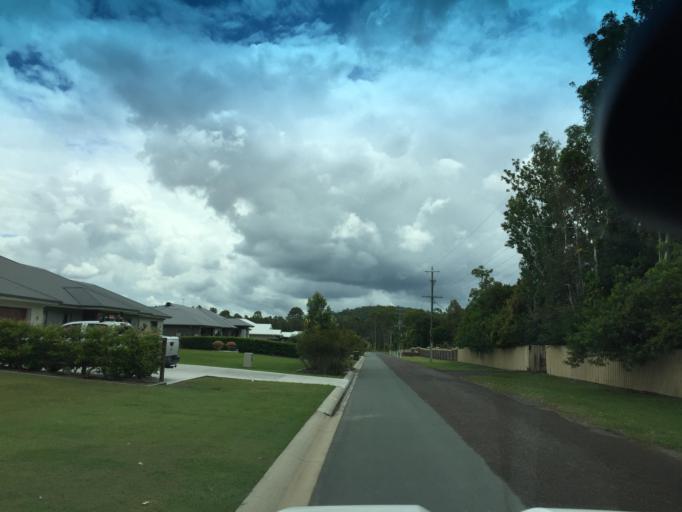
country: AU
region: Queensland
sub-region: Moreton Bay
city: Caboolture
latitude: -27.0426
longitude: 152.9298
